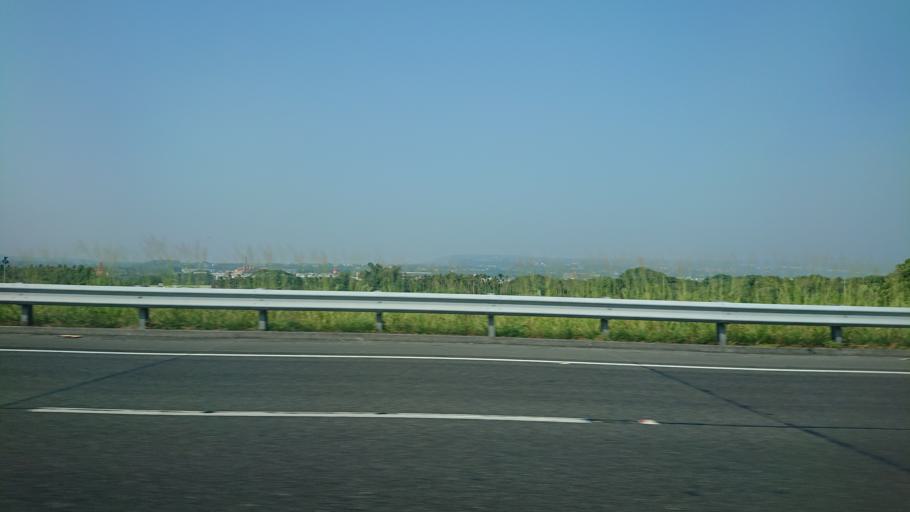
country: TW
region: Taiwan
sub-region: Nantou
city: Nantou
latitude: 23.8681
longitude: 120.7043
